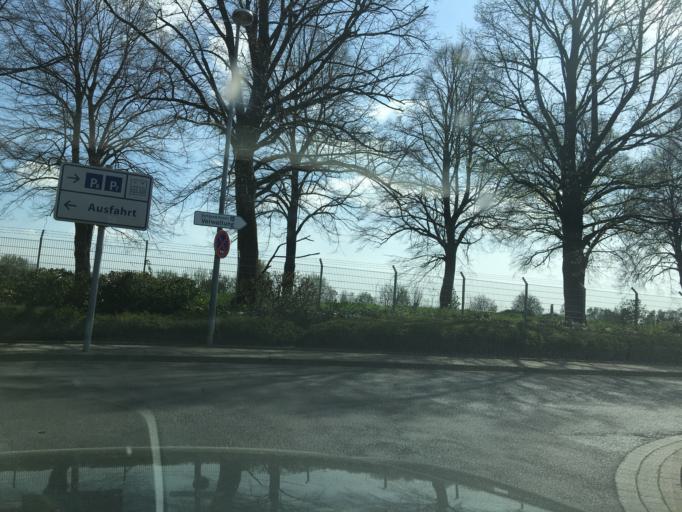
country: DE
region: North Rhine-Westphalia
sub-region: Regierungsbezirk Arnsberg
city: Holzwickede
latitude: 51.5111
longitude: 7.6050
